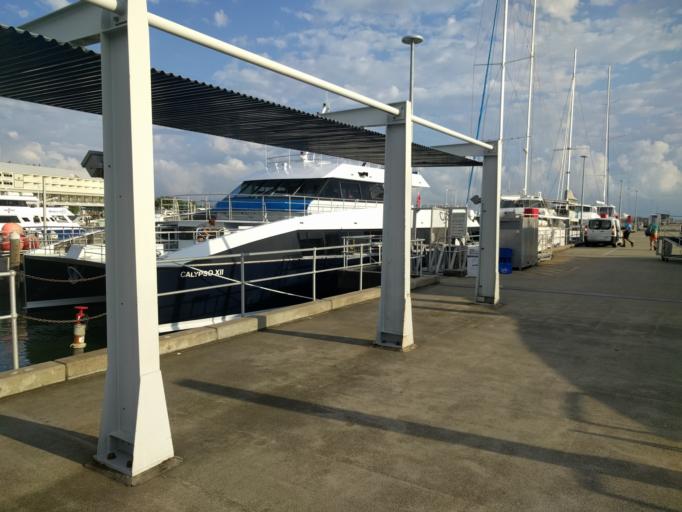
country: AU
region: Queensland
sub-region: Cairns
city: Cairns
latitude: -16.9210
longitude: 145.7824
